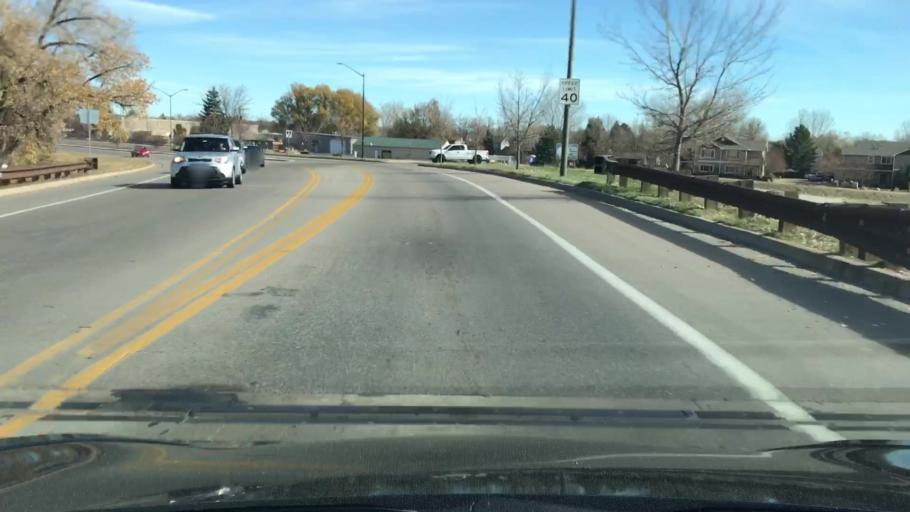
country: US
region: Colorado
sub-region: Larimer County
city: Fort Collins
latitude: 40.5782
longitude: -105.0346
